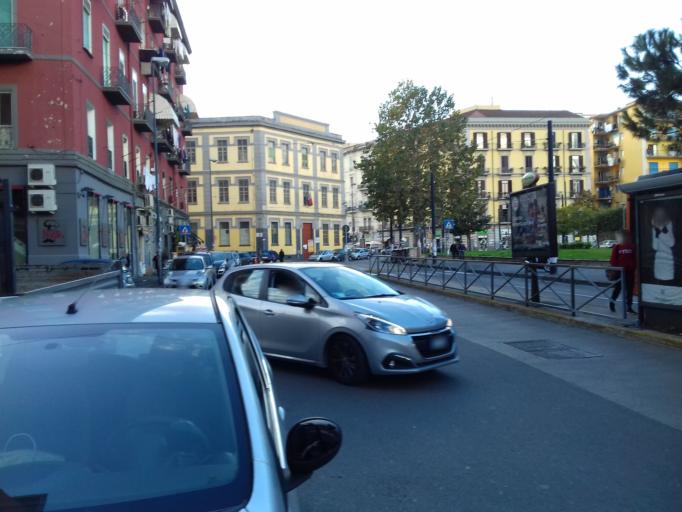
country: IT
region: Campania
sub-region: Provincia di Napoli
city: Napoli
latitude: 40.8578
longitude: 14.2739
